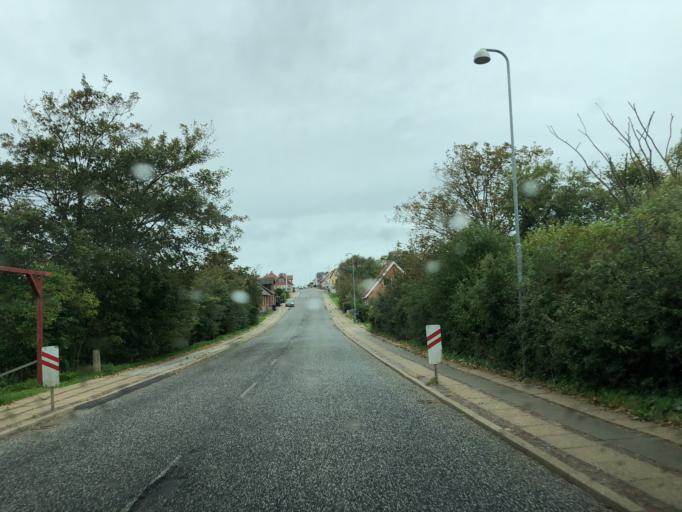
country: DK
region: North Denmark
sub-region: Thisted Kommune
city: Hurup
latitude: 56.7128
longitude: 8.4010
